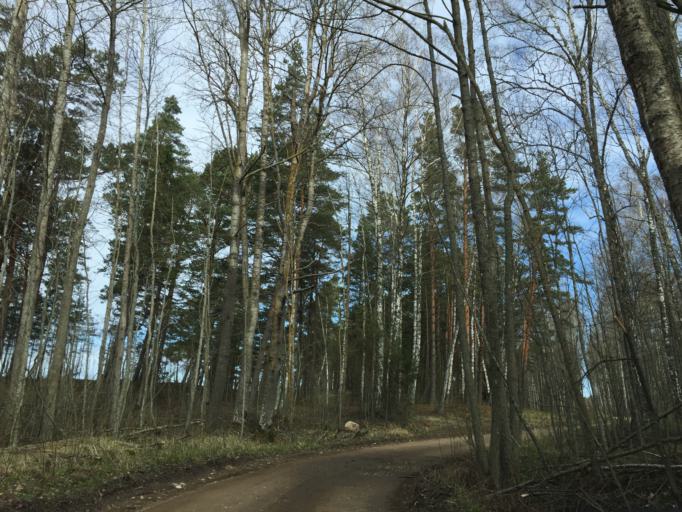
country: LV
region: Salacgrivas
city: Salacgriva
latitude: 57.5855
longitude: 24.3701
